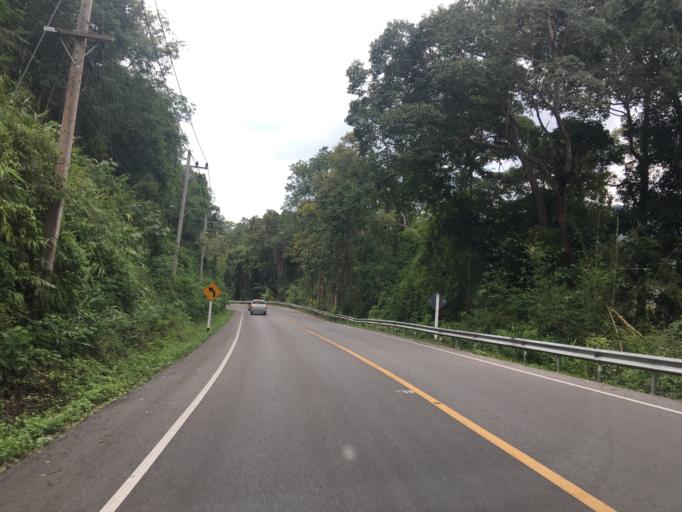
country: TH
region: Nan
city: Ban Luang
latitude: 18.8735
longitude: 100.5172
